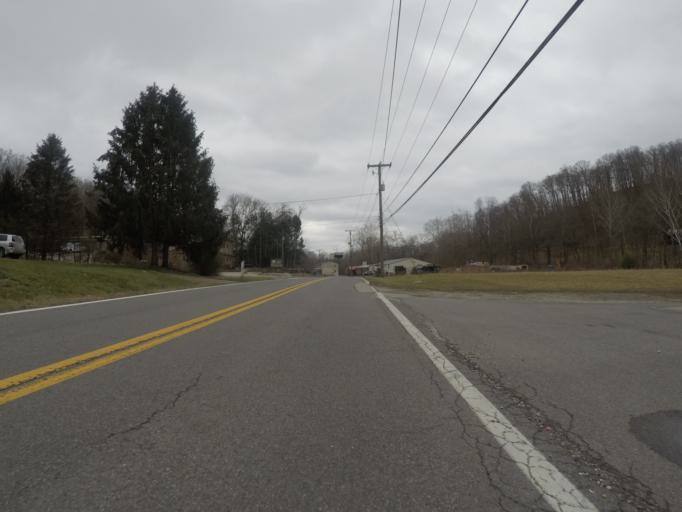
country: US
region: West Virginia
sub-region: Cabell County
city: Barboursville
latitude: 38.4264
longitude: -82.2918
